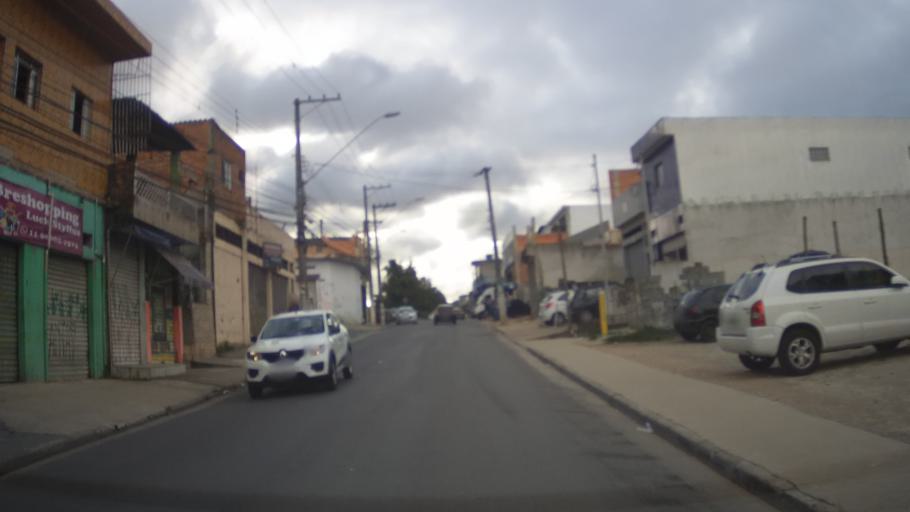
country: BR
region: Sao Paulo
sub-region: Itaquaquecetuba
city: Itaquaquecetuba
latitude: -23.4639
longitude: -46.3994
